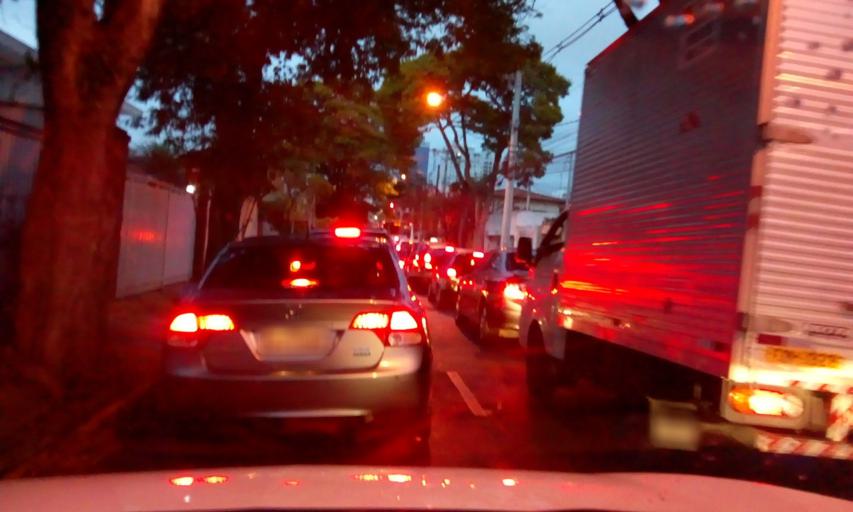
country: BR
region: Sao Paulo
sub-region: Sao Paulo
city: Sao Paulo
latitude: -23.6061
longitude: -46.6816
